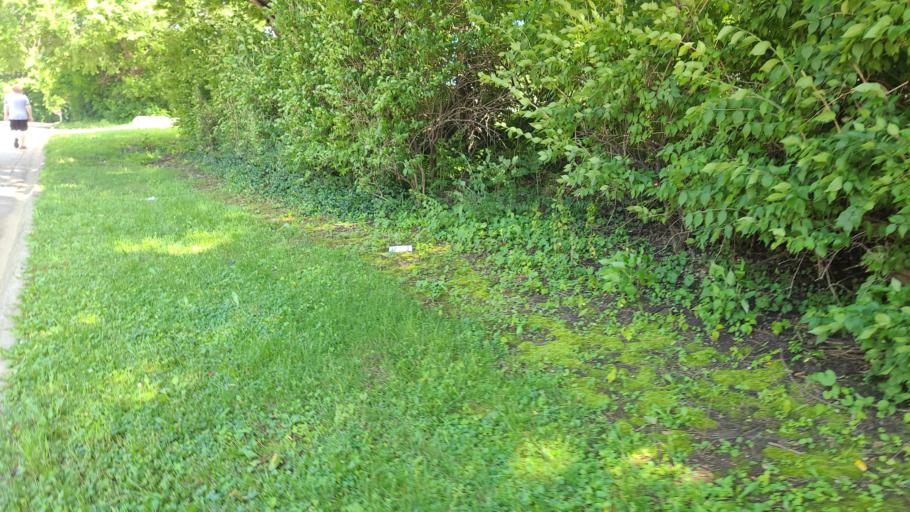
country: US
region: Kansas
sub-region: Douglas County
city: Lawrence
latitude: 38.9696
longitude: -95.2875
